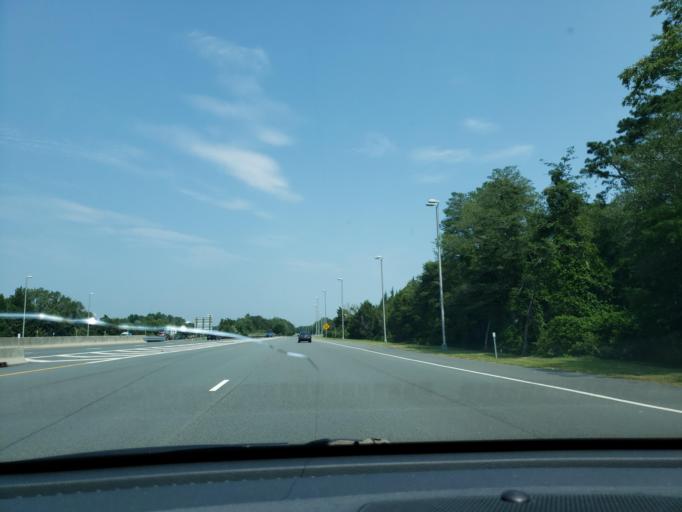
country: US
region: New Jersey
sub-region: Cape May County
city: Sea Isle City
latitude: 39.1942
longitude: -74.7092
